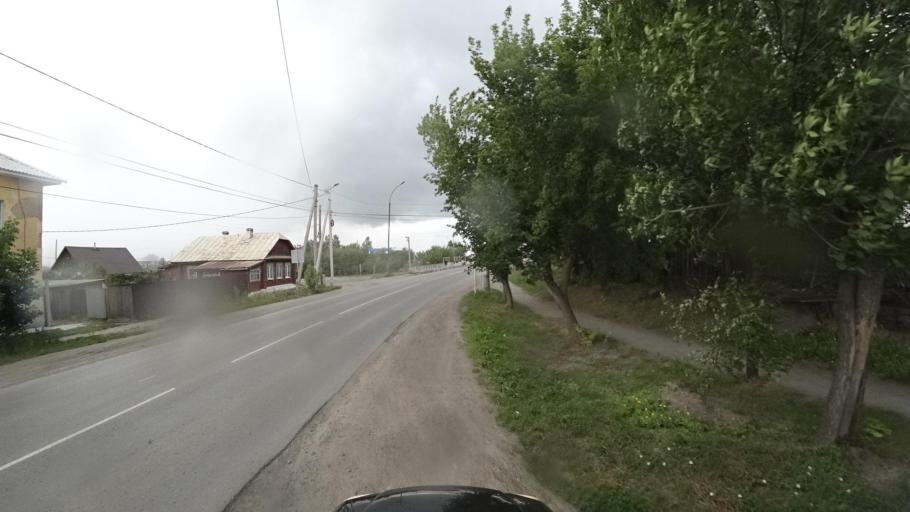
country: RU
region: Sverdlovsk
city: Kamyshlov
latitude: 56.8499
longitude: 62.7004
